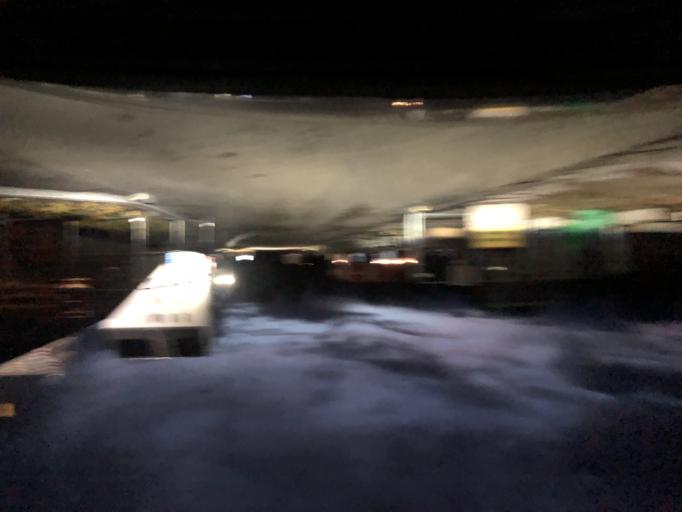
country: SE
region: Gaevleborg
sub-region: Gavle Kommun
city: Gavle
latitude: 60.6669
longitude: 17.1111
